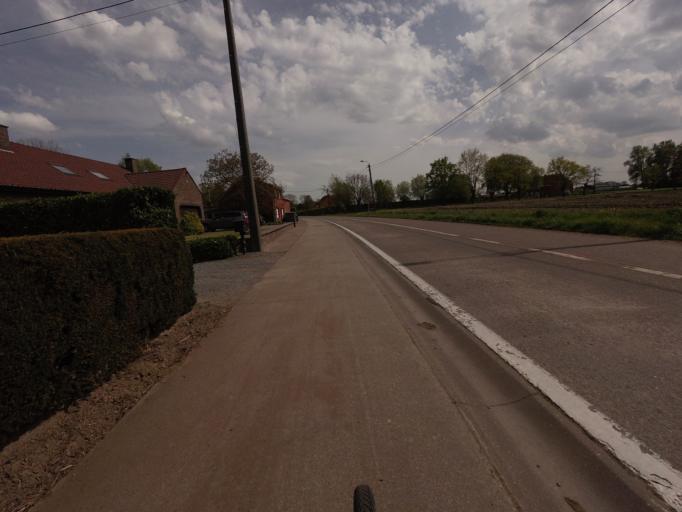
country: BE
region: Flanders
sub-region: Provincie Antwerpen
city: Putte
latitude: 51.0720
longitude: 4.6036
